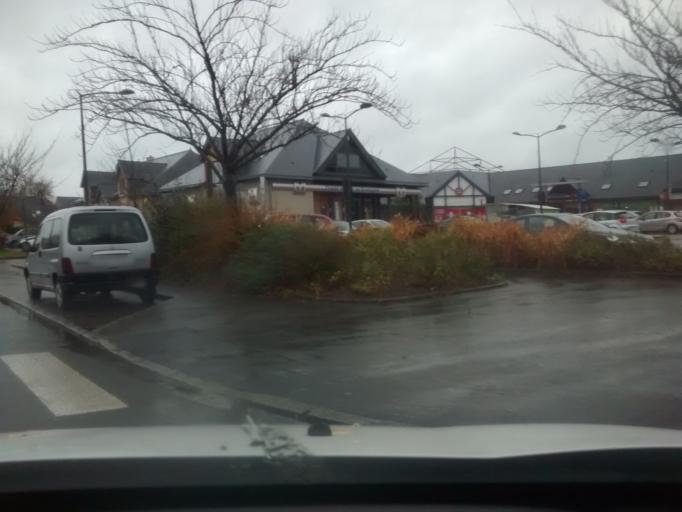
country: FR
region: Brittany
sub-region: Departement d'Ille-et-Vilaine
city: Fouillard
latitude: 48.1583
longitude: -1.5798
